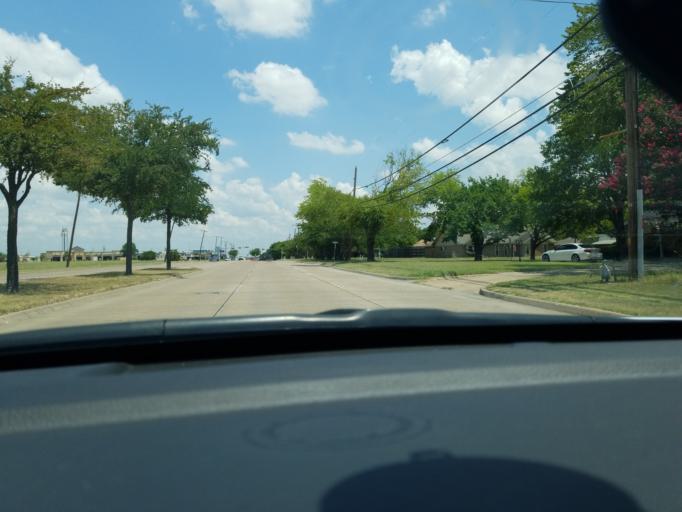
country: US
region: Texas
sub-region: Dallas County
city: Sunnyvale
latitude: 32.8202
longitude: -96.5957
